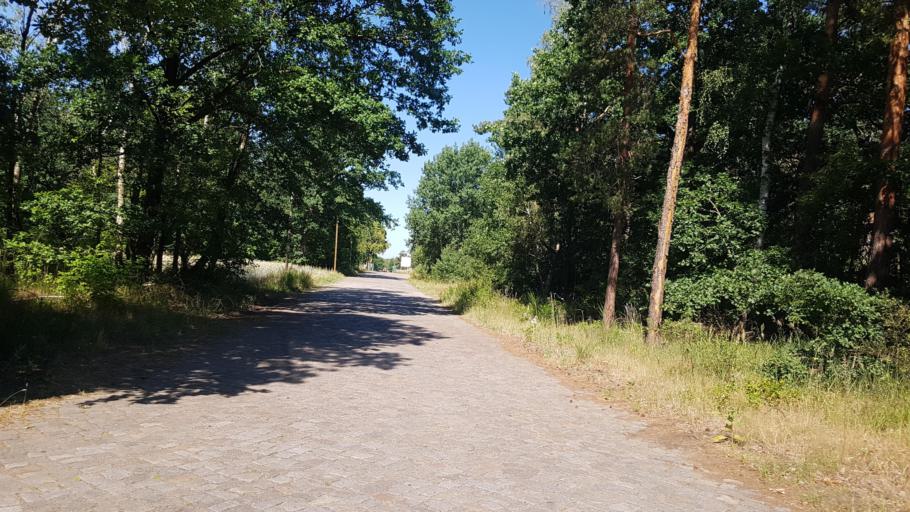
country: DE
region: Brandenburg
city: Niedergorsdorf
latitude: 52.0050
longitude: 12.9643
